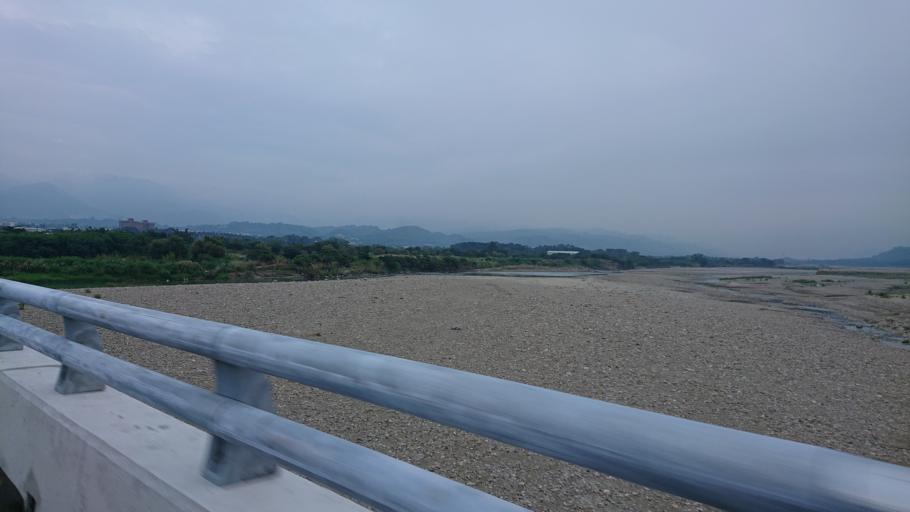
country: TW
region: Taiwan
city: Lugu
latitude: 23.7595
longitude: 120.6559
